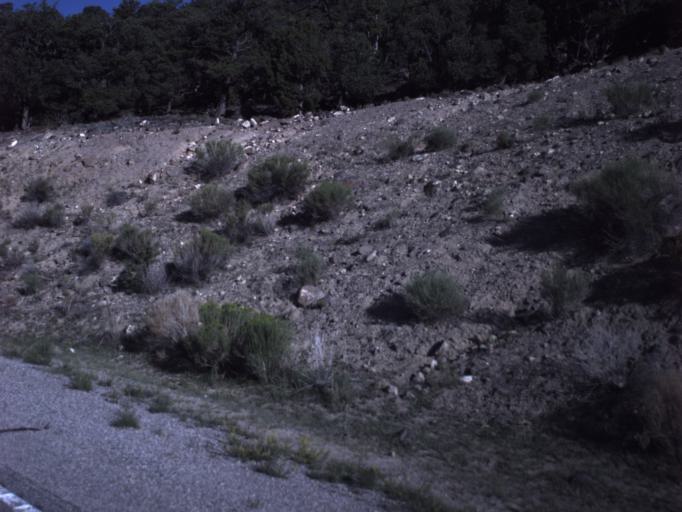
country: US
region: Utah
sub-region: Wayne County
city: Loa
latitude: 38.6756
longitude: -111.4045
